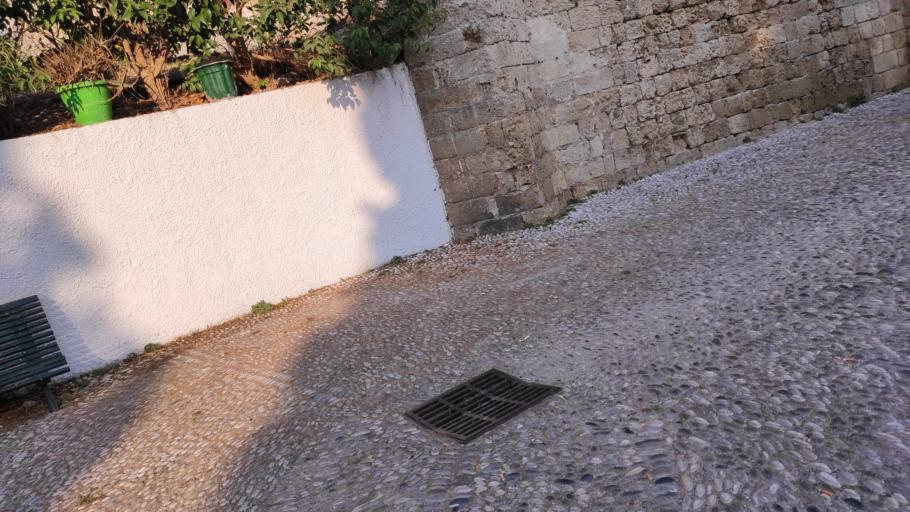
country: GR
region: South Aegean
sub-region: Nomos Dodekanisou
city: Rodos
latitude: 36.4427
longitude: 28.2308
